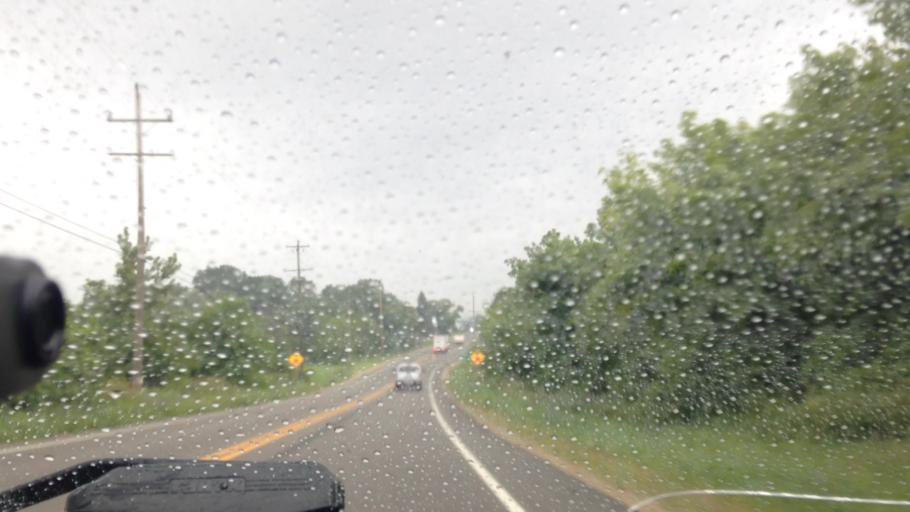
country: US
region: Wisconsin
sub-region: Washington County
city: Richfield
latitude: 43.2838
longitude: -88.2131
